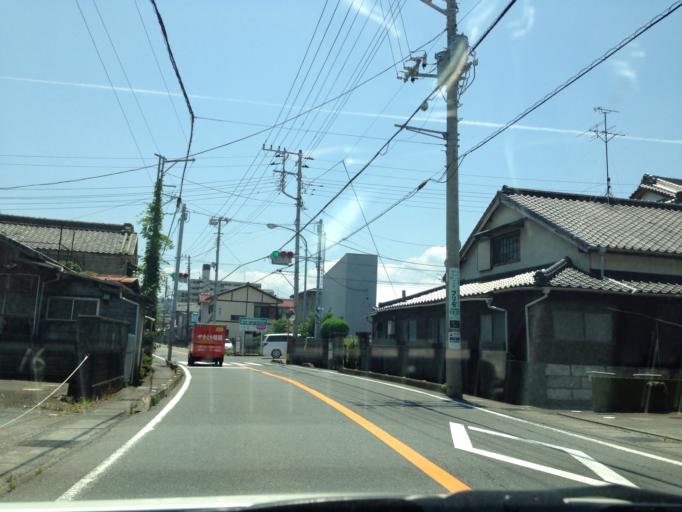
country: JP
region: Shizuoka
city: Numazu
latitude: 35.0652
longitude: 138.8785
